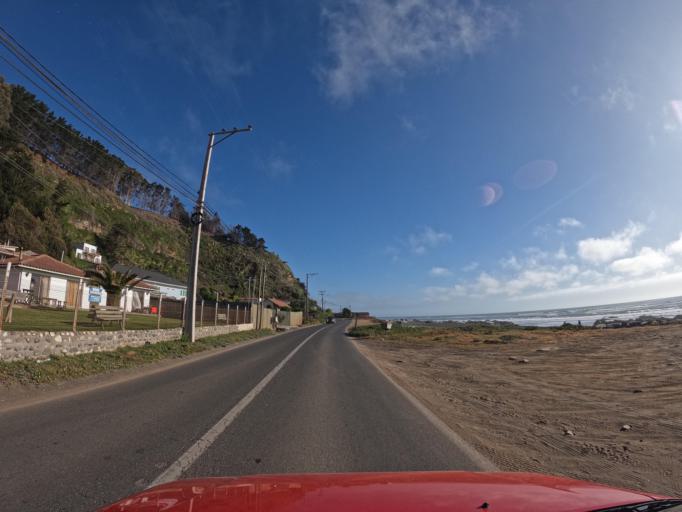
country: CL
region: Maule
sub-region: Provincia de Talca
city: Constitucion
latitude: -34.9134
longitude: -72.1818
